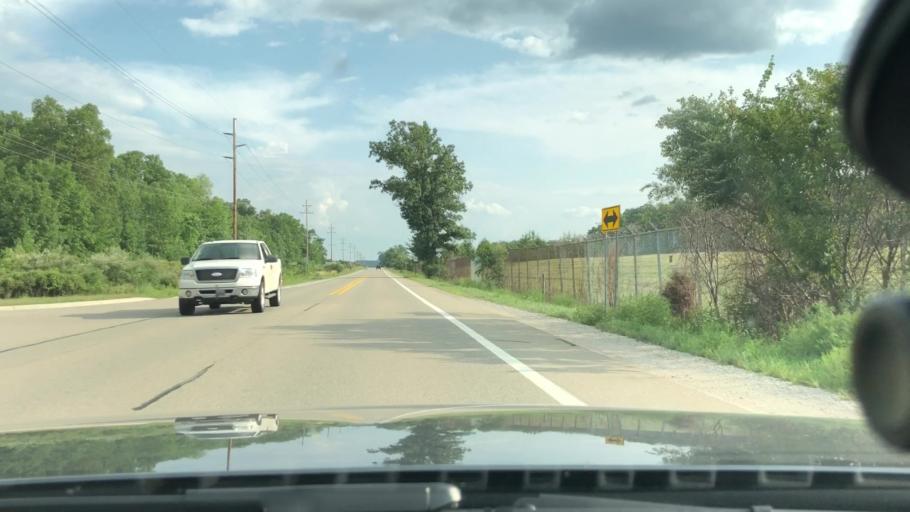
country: US
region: Michigan
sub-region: Washtenaw County
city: Chelsea
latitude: 42.2656
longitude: -84.0342
